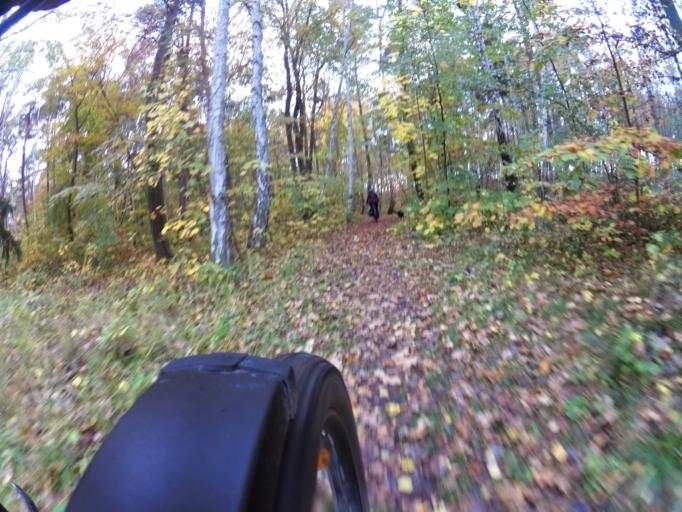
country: PL
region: Pomeranian Voivodeship
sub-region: Powiat pucki
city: Jastarnia
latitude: 54.7164
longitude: 18.6349
